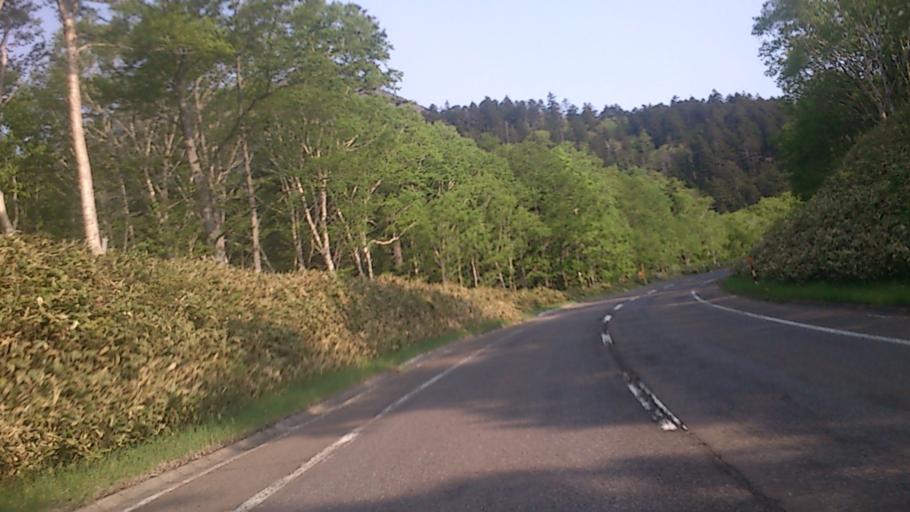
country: JP
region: Hokkaido
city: Bihoro
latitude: 43.4394
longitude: 144.1855
